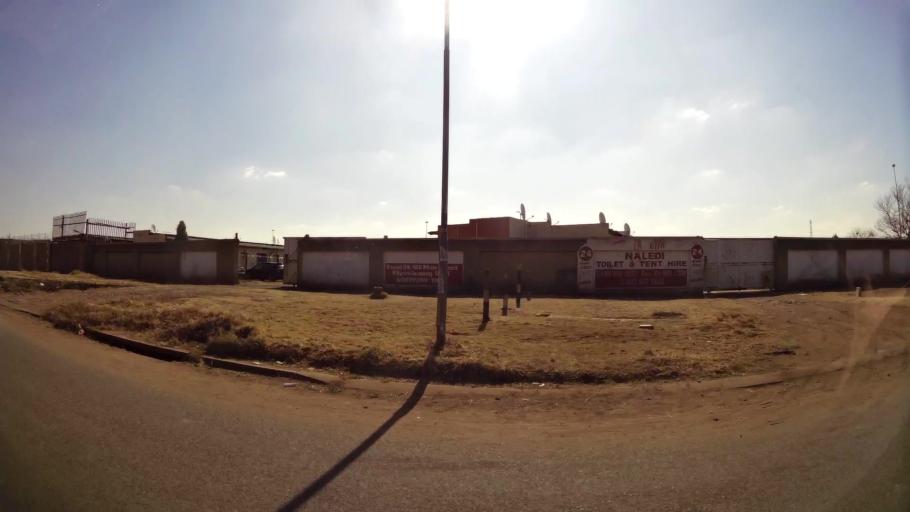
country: ZA
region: Gauteng
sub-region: City of Johannesburg Metropolitan Municipality
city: Soweto
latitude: -26.2921
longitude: 27.8537
